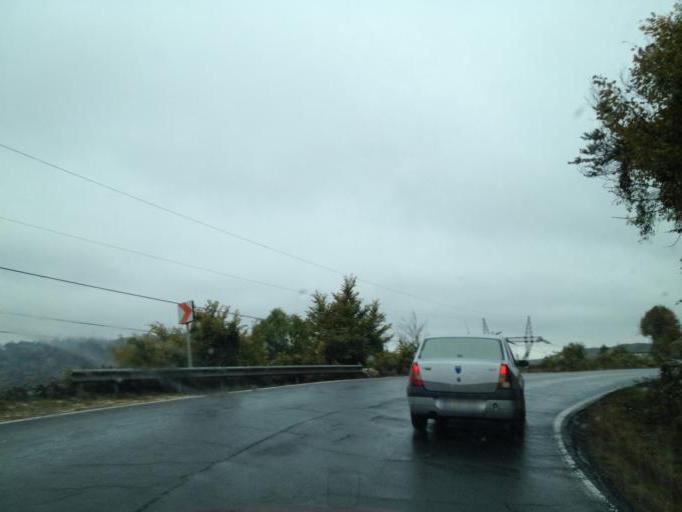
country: RO
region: Arges
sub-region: Comuna Dragoslavele
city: Dragoslavele
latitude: 45.3007
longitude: 25.1537
